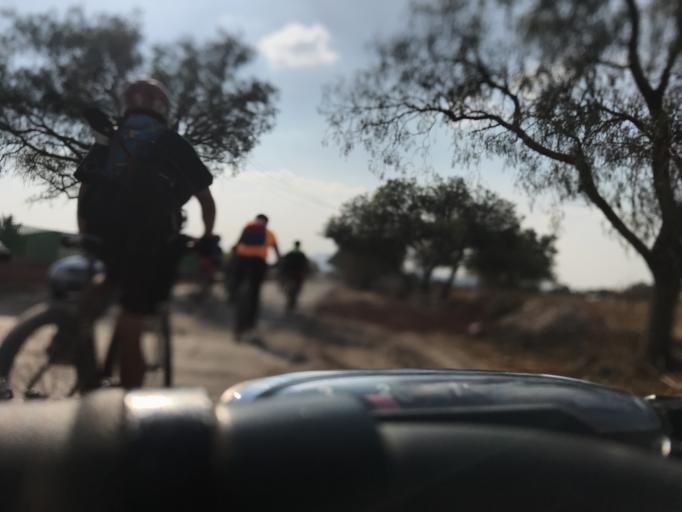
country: MX
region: Morelos
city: Santiago Atlatongo
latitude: 19.6794
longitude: -98.9055
